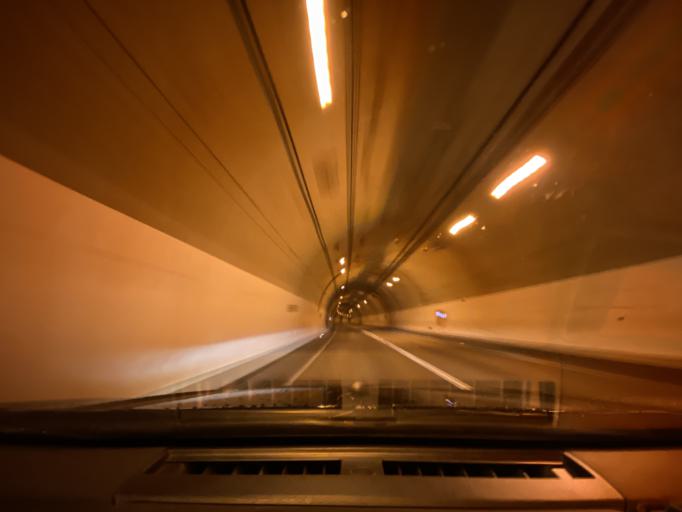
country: JP
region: Hokkaido
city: Ishikari
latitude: 43.4688
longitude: 141.3975
